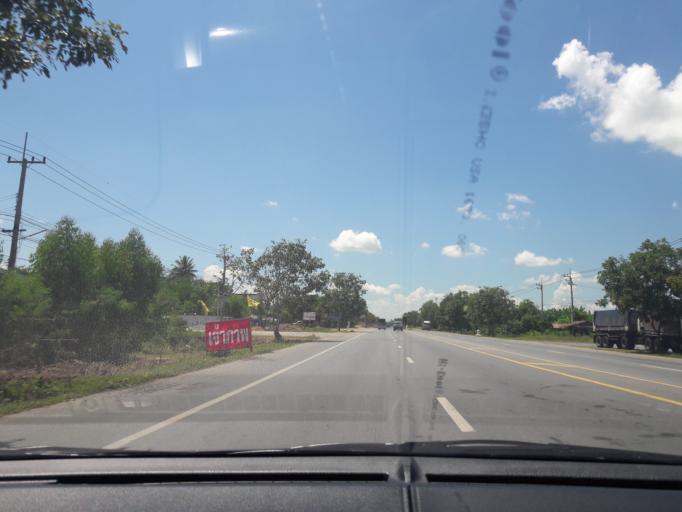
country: TH
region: Kanchanaburi
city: Tha Maka
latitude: 14.0327
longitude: 99.8262
